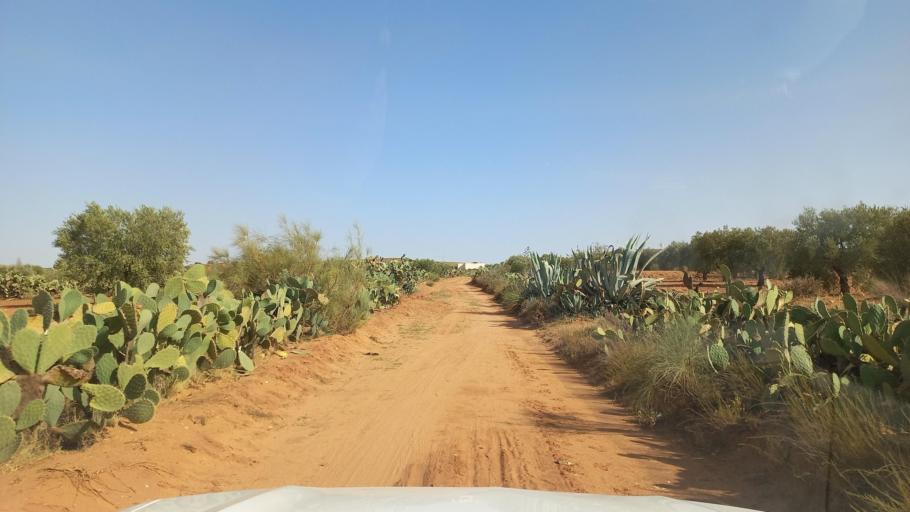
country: TN
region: Al Qasrayn
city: Kasserine
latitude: 35.2024
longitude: 8.9645
